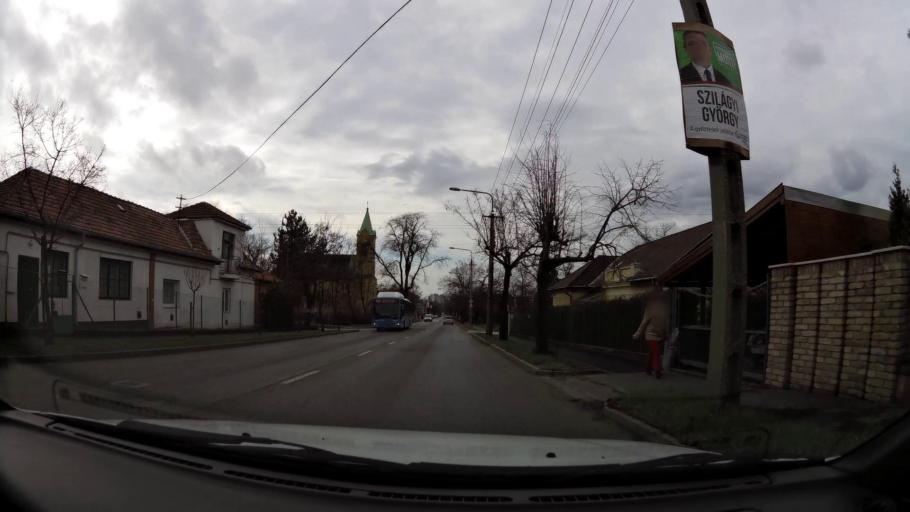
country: HU
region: Budapest
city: Budapest XVII. keruelet
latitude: 47.4911
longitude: 19.2599
